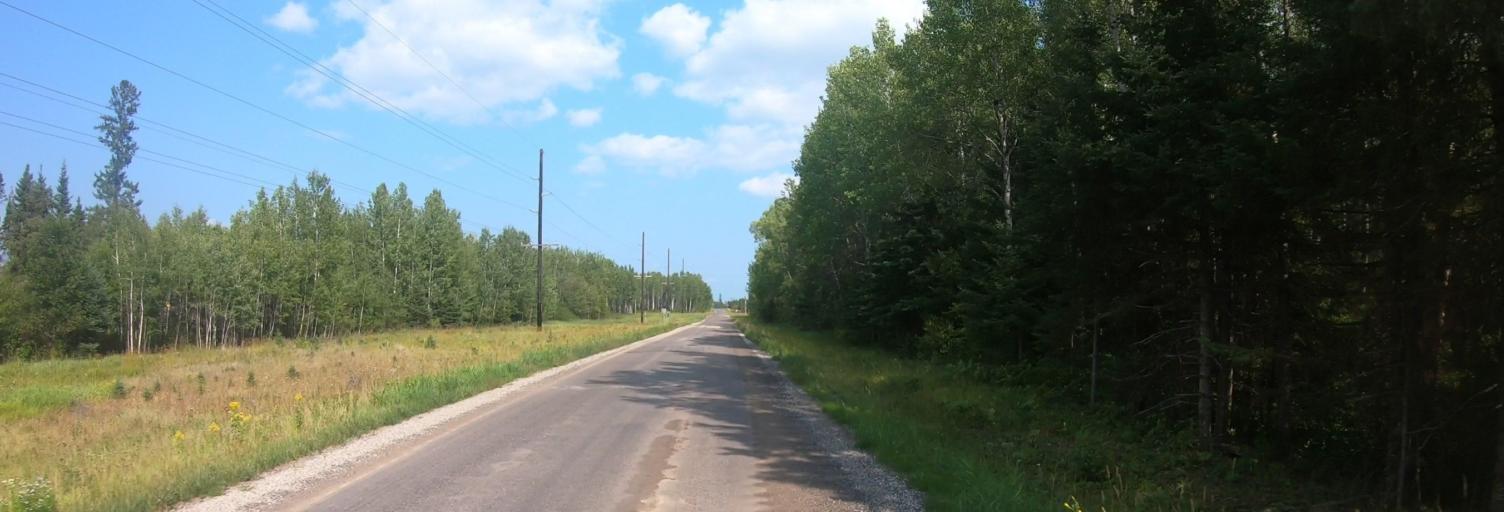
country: US
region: Minnesota
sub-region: Saint Louis County
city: Mountain Iron
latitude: 47.8920
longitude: -92.7223
